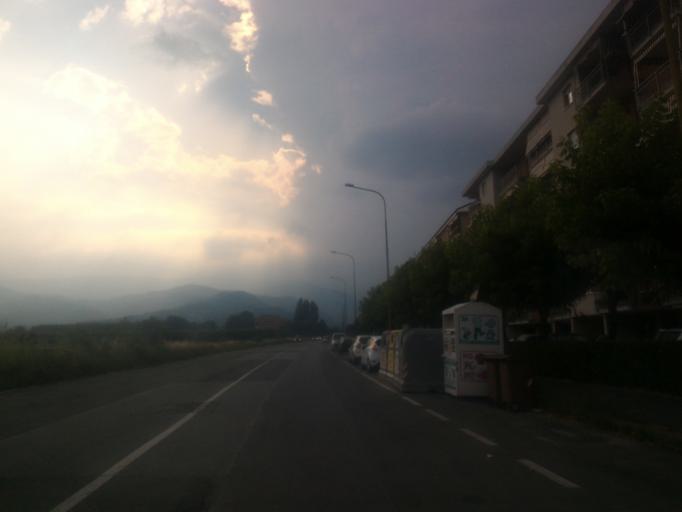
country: IT
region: Piedmont
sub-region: Provincia di Torino
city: Pinerolo
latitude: 44.8763
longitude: 7.3323
